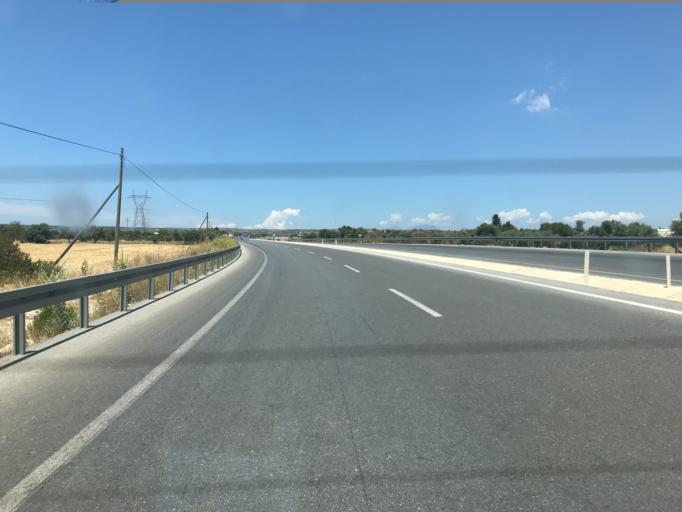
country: TR
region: Aydin
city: Akkoy
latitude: 37.4457
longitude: 27.3536
